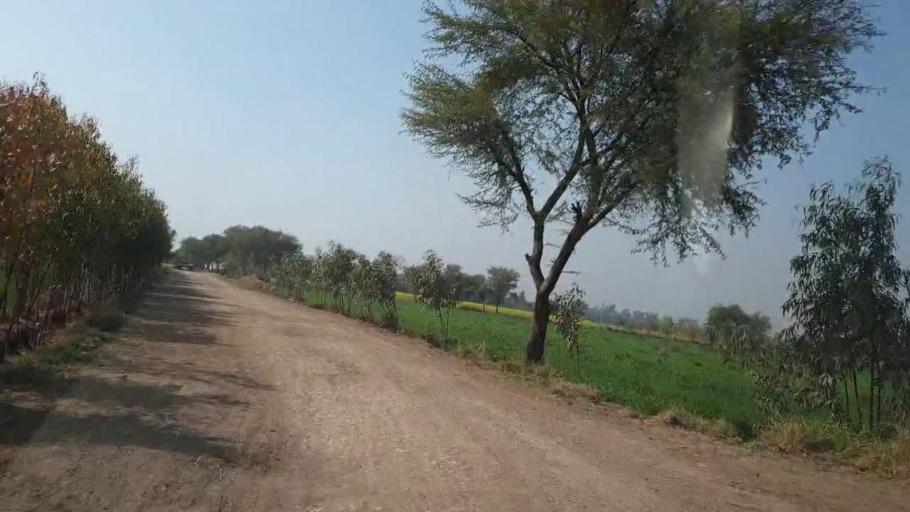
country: PK
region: Sindh
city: Matiari
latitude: 25.5428
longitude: 68.4651
